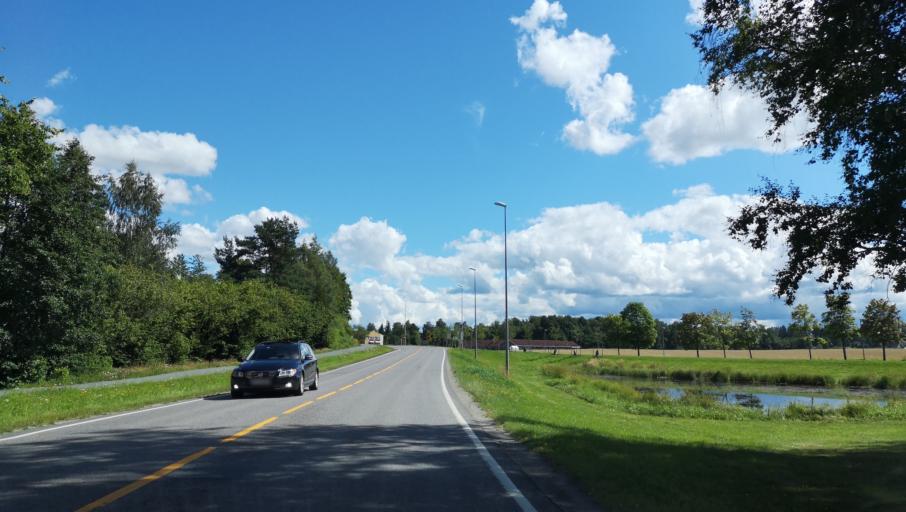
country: NO
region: Akershus
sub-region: As
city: As
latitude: 59.6648
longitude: 10.7794
